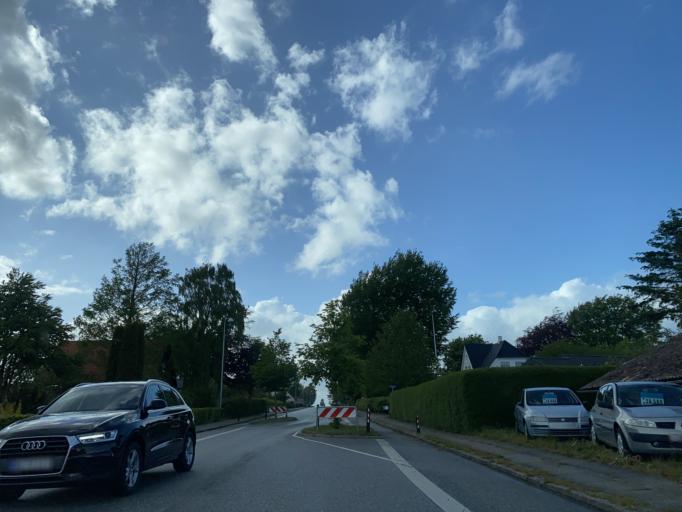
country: DK
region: Central Jutland
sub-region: Horsens Kommune
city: Horsens
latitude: 55.8917
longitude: 9.7734
